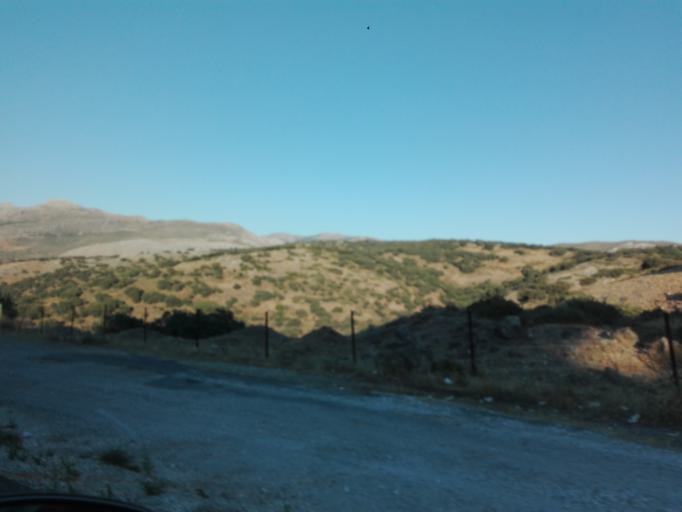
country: ES
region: Andalusia
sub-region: Provincia de Malaga
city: Ronda
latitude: 36.7097
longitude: -5.1324
